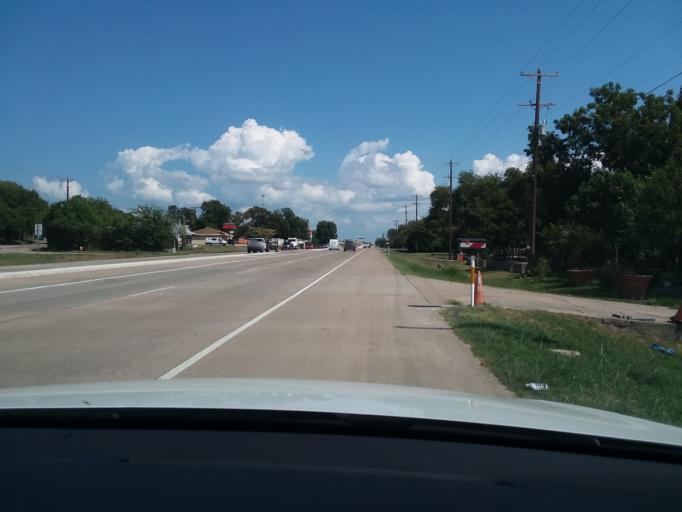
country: US
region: Texas
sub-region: Collin County
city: Lowry Crossing
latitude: 33.1939
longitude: -96.5579
